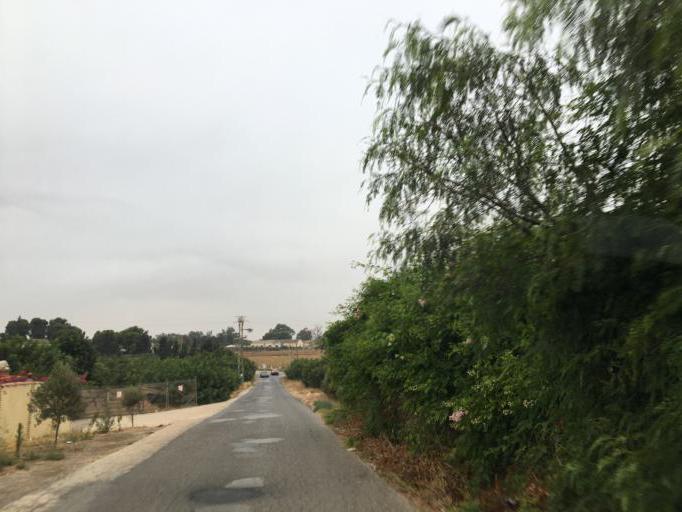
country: ES
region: Murcia
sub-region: Murcia
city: Cartagena
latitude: 37.6624
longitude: -1.0074
